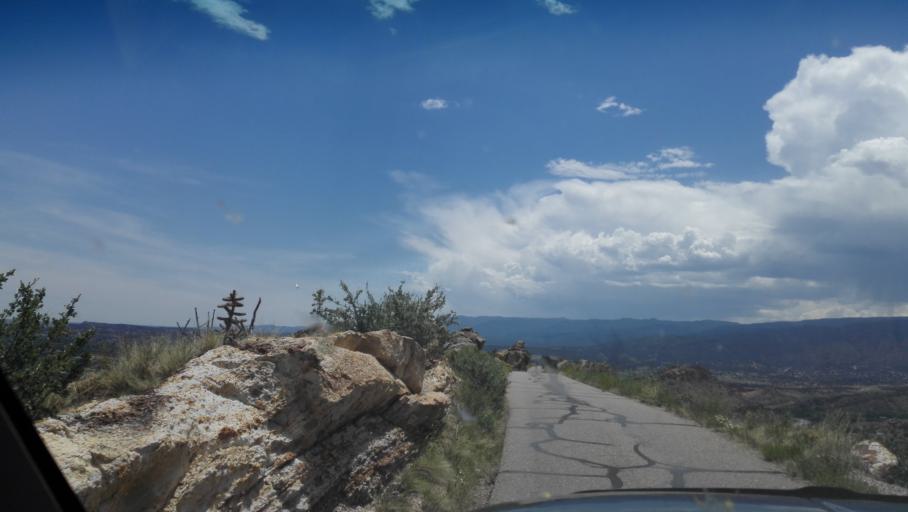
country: US
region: Colorado
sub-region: Fremont County
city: Canon City
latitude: 38.4599
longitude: -105.2511
